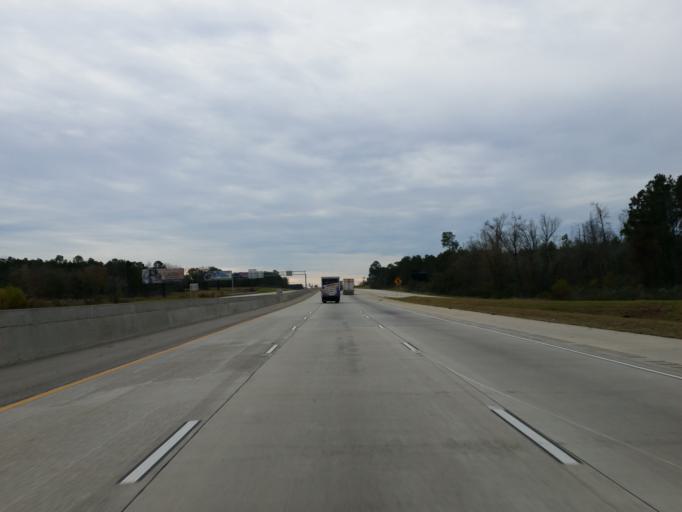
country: US
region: Georgia
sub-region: Tift County
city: Unionville
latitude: 31.3556
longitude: -83.4894
